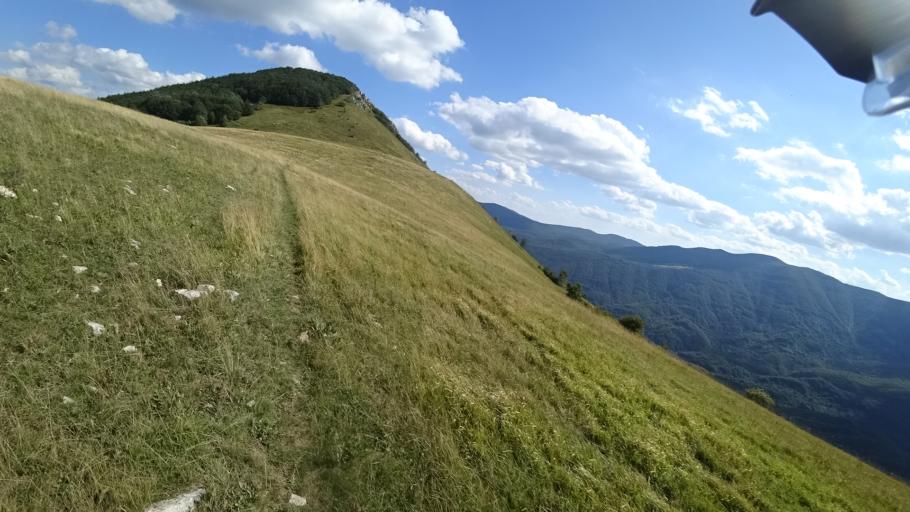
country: HR
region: Zadarska
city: Gracac
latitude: 44.3850
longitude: 16.0449
